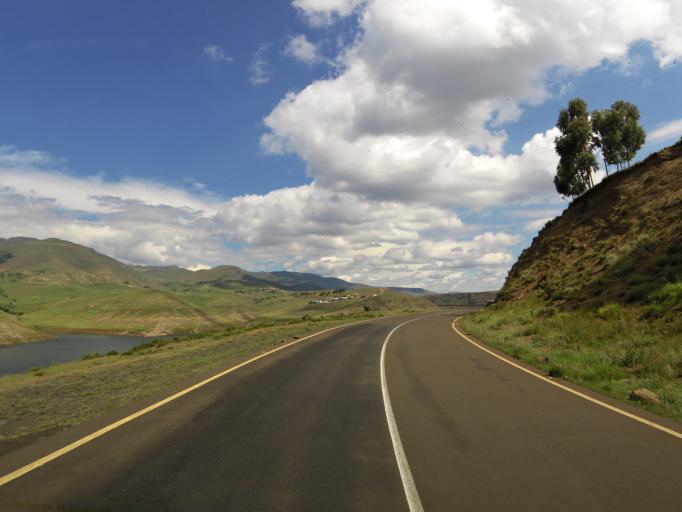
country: LS
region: Thaba-Tseka
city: Thaba-Tseka
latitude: -29.1667
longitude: 28.4833
